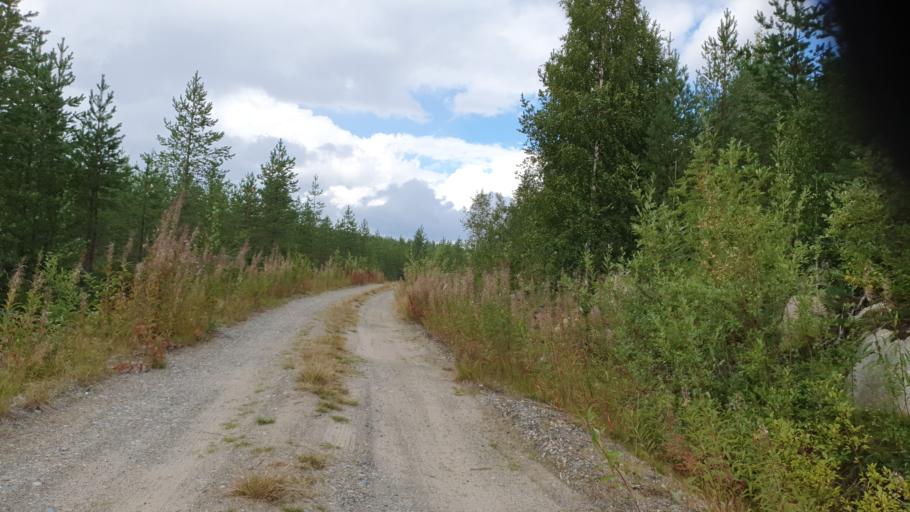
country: FI
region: Kainuu
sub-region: Kehys-Kainuu
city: Kuhmo
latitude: 64.1455
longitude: 29.3875
